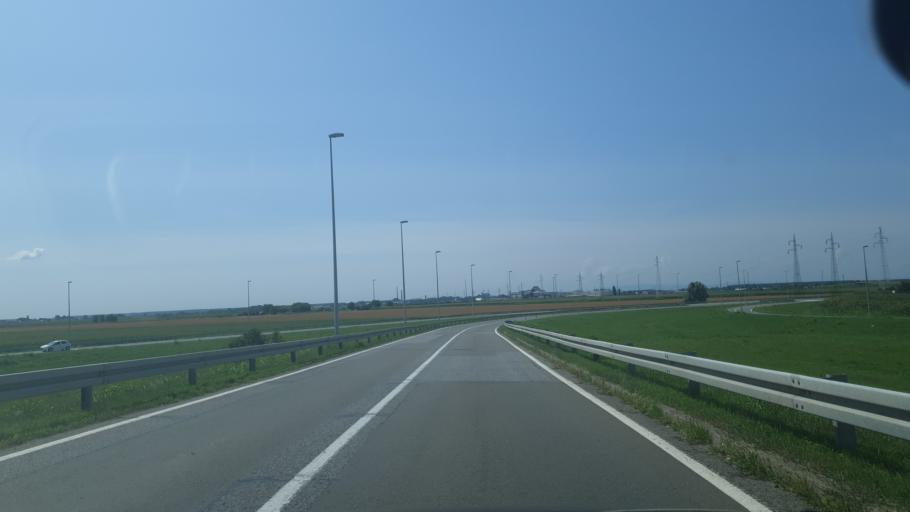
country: RS
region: Autonomna Pokrajina Vojvodina
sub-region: Sremski Okrug
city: Sremska Mitrovica
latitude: 44.9979
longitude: 19.6506
